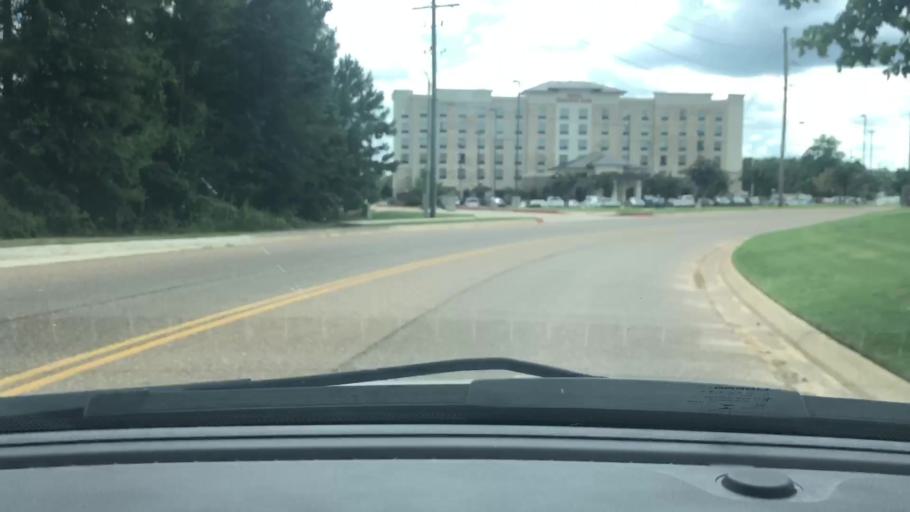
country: US
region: Arkansas
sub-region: Miller County
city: Texarkana
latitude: 33.4593
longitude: -94.0741
